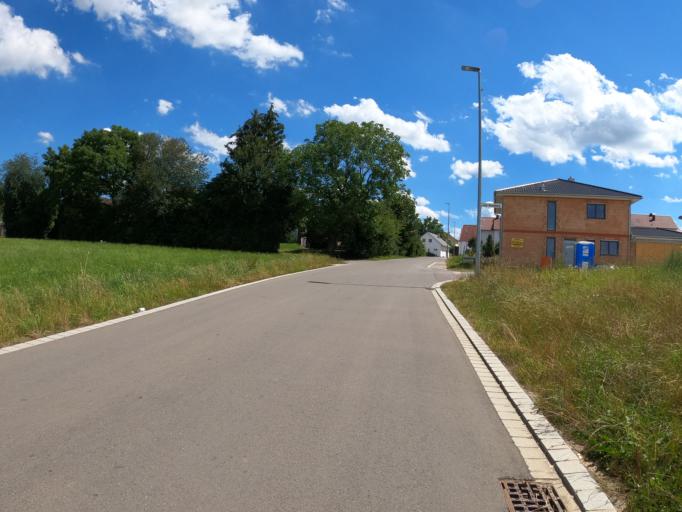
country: DE
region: Bavaria
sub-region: Swabia
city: Leipheim
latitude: 48.4019
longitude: 10.1934
